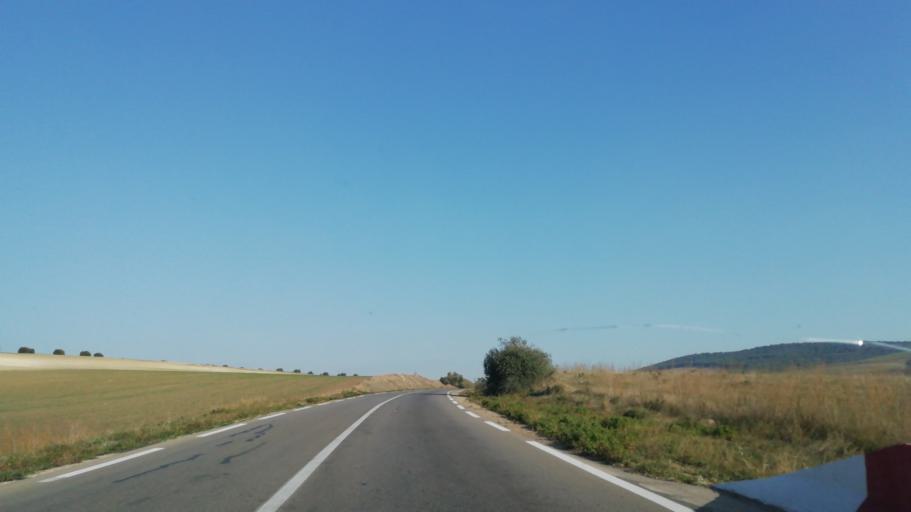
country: DZ
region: Ain Temouchent
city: Hammam Bou Hadjar
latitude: 35.1700
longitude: -0.9054
